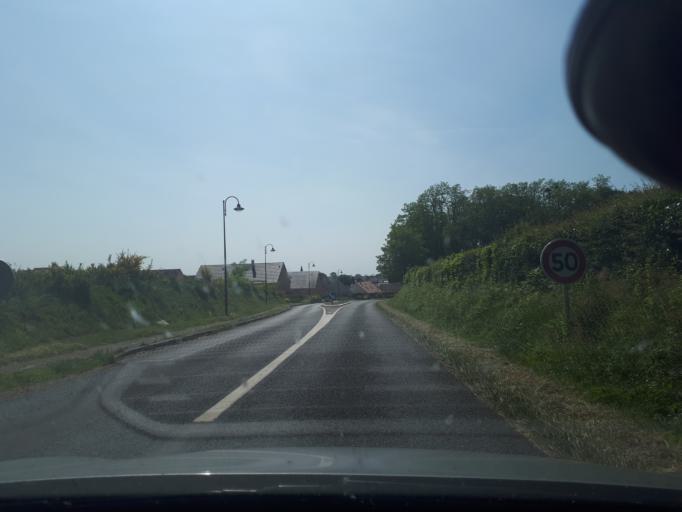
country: FR
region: Pays de la Loire
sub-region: Departement de la Sarthe
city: Champagne
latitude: 48.0708
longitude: 0.3399
